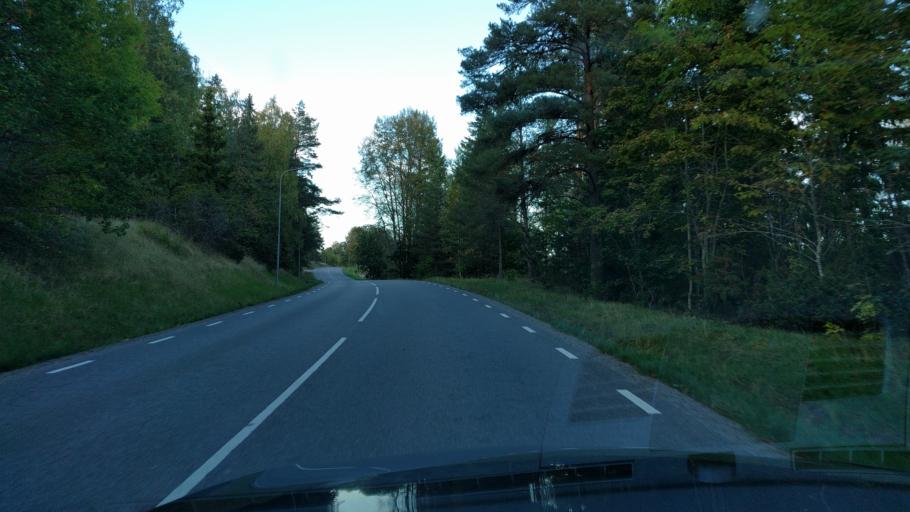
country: SE
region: Uppsala
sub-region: Tierps Kommun
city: Orbyhus
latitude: 60.1684
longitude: 17.6108
